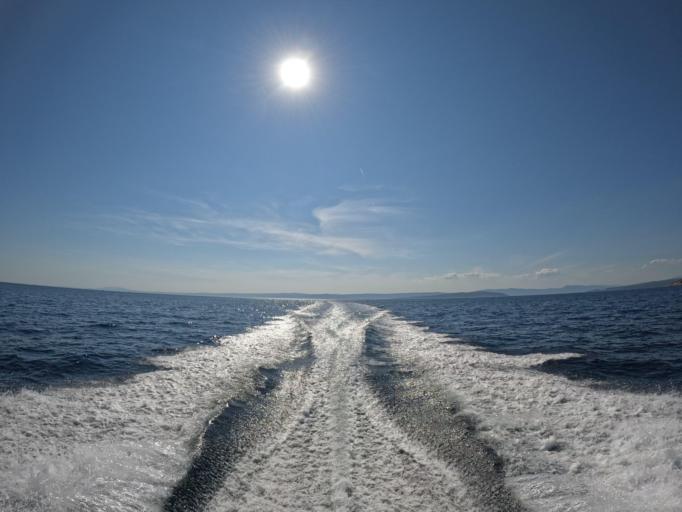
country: HR
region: Primorsko-Goranska
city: Punat
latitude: 44.9602
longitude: 14.6456
